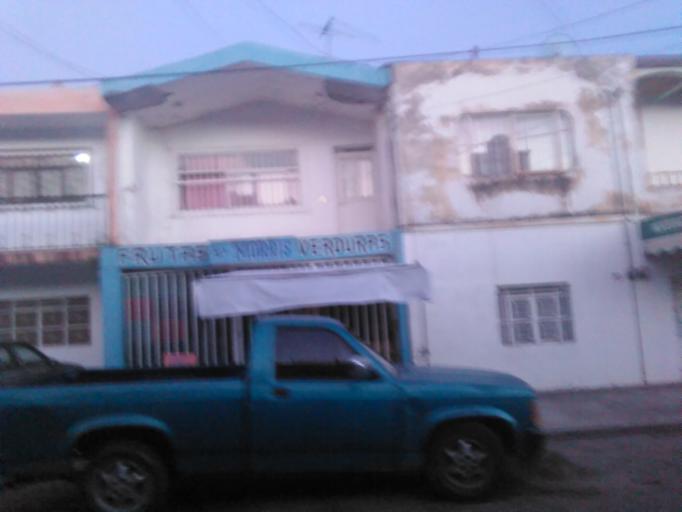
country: MX
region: Nayarit
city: Tepic
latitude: 21.4859
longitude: -104.8920
